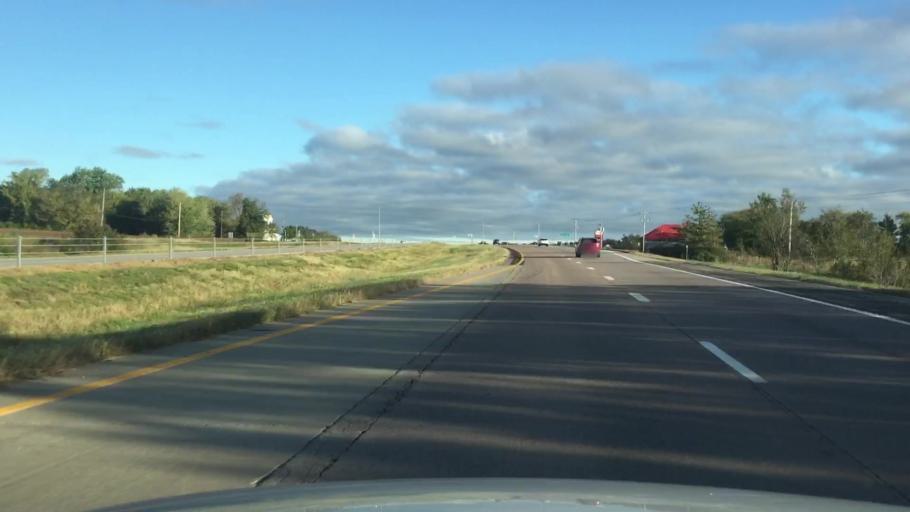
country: US
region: Missouri
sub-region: Boone County
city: Ashland
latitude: 38.8585
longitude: -92.2491
